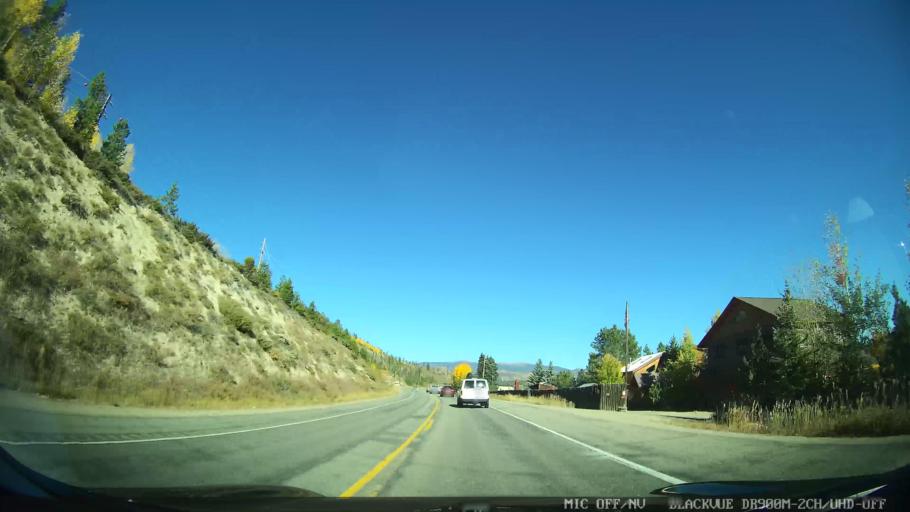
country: US
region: Colorado
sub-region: Grand County
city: Granby
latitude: 40.1581
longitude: -105.8910
